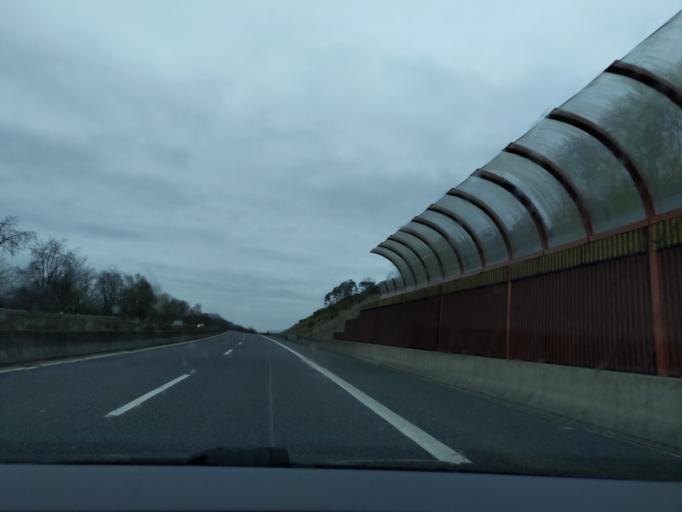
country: DE
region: Hesse
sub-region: Regierungsbezirk Giessen
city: Fronhausen
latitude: 50.7369
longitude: 8.7375
